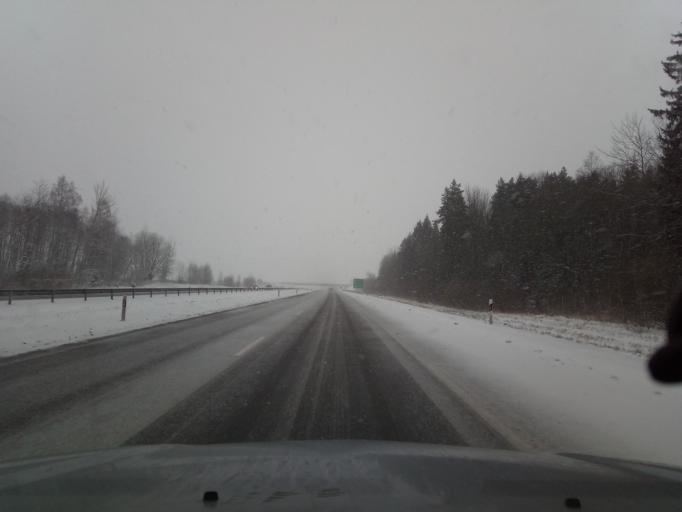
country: LT
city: Sirvintos
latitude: 54.9523
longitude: 24.9620
